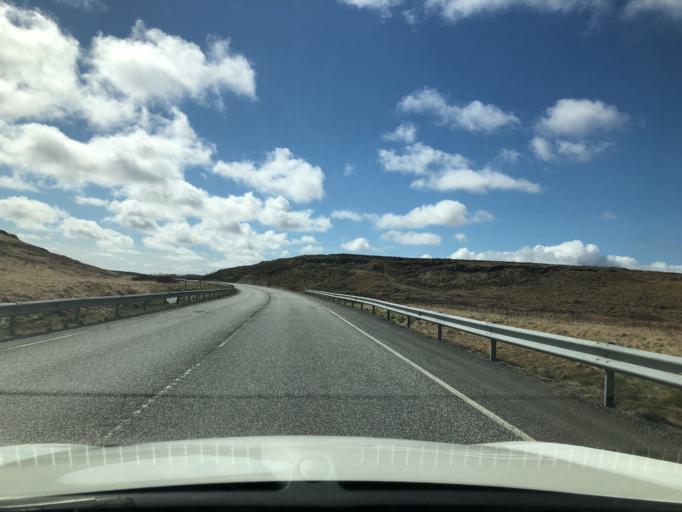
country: IS
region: South
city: Selfoss
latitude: 63.9476
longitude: -20.7490
